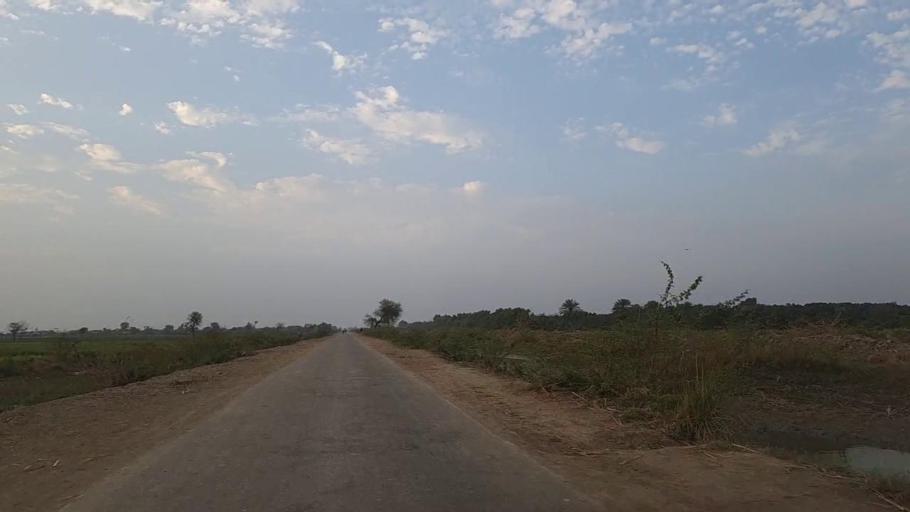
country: PK
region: Sindh
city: Mirwah Gorchani
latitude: 25.3205
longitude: 69.2197
